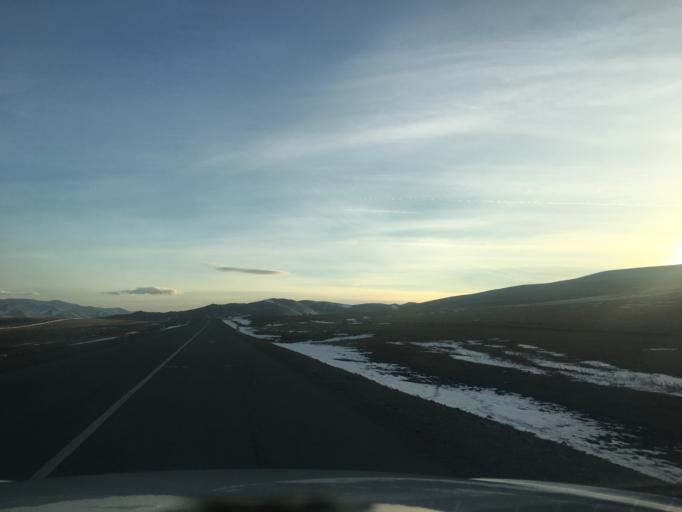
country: MN
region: Central Aimak
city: Mandal
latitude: 48.2210
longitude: 106.7132
